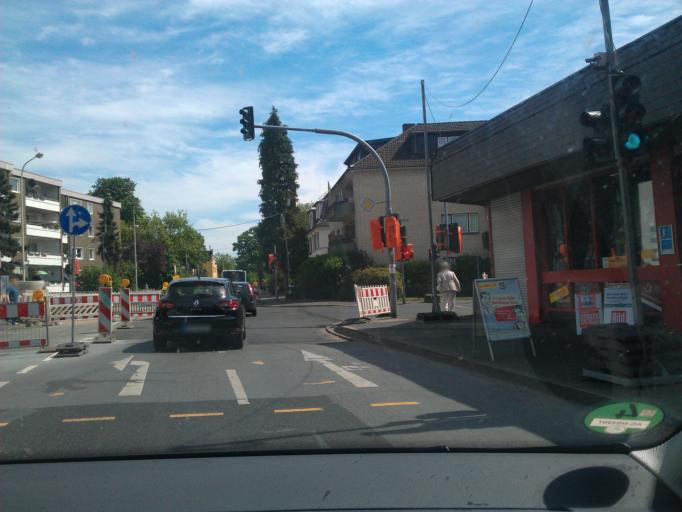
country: DE
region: North Rhine-Westphalia
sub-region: Regierungsbezirk Dusseldorf
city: Hilden
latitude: 51.1629
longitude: 6.9409
